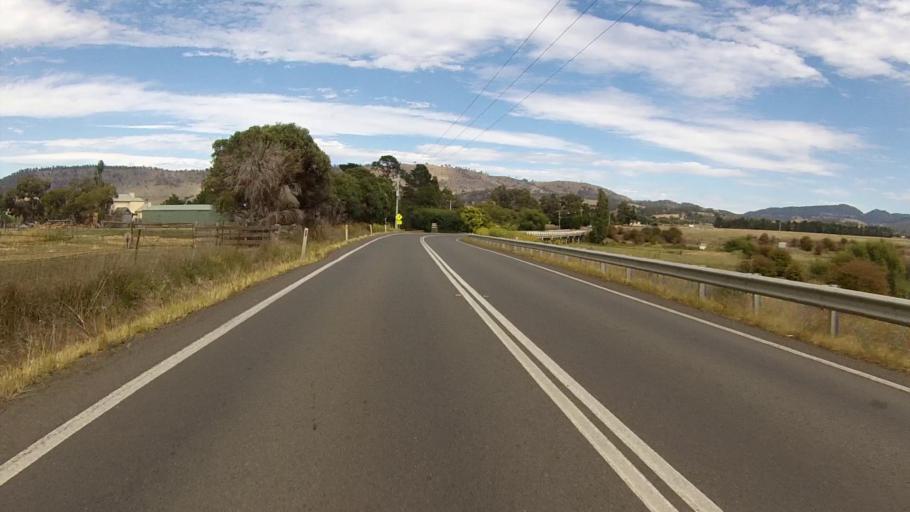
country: AU
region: Tasmania
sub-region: Clarence
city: Cambridge
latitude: -42.6891
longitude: 147.4395
